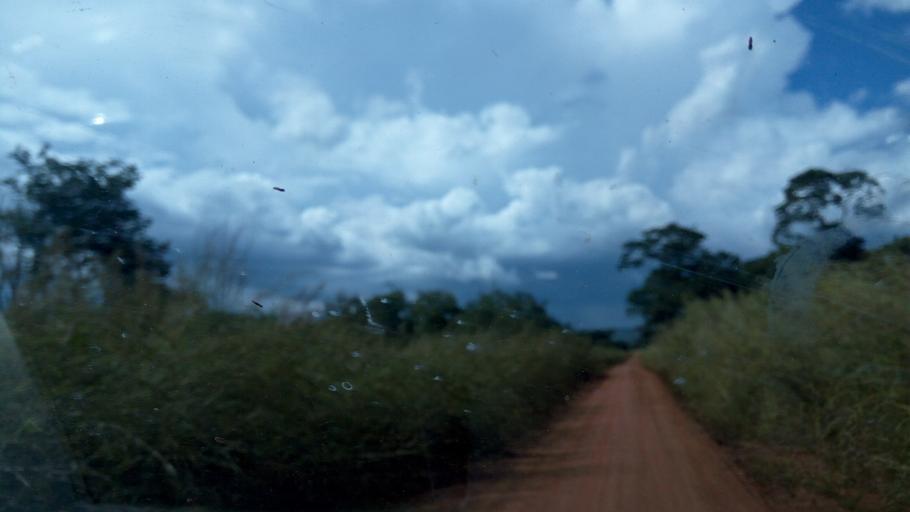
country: ZM
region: Northern
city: Kaputa
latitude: -8.1726
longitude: 29.0911
